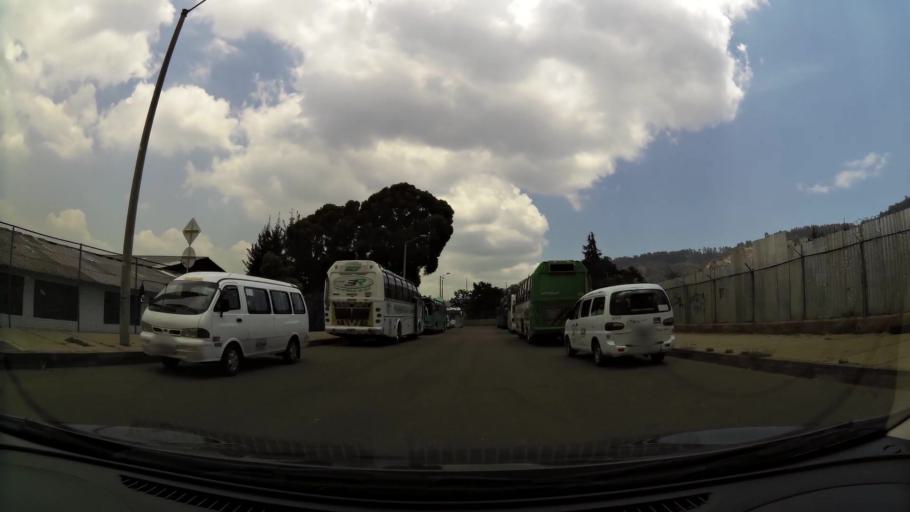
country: CO
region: Cundinamarca
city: La Calera
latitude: 4.7462
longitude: -74.0253
